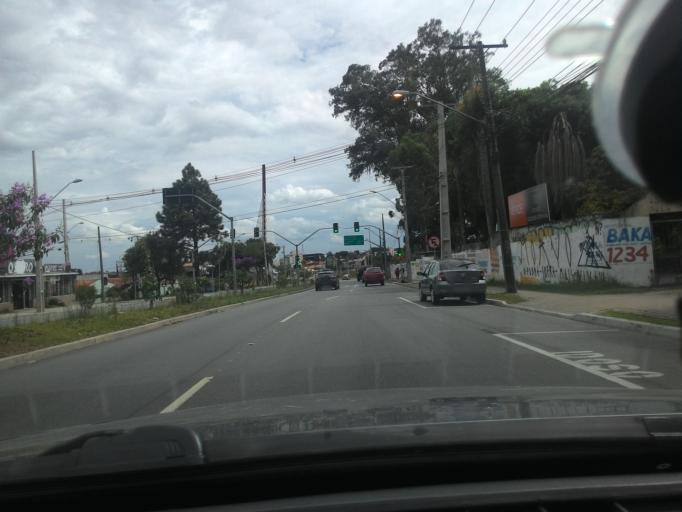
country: BR
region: Parana
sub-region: Pinhais
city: Pinhais
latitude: -25.4613
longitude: -49.2338
